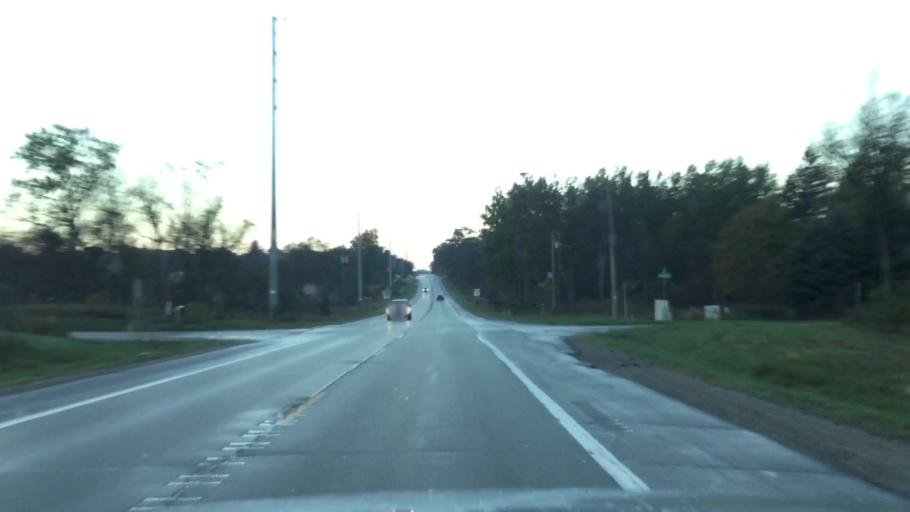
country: US
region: Michigan
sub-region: Livingston County
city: Howell
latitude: 42.6303
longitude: -83.8554
